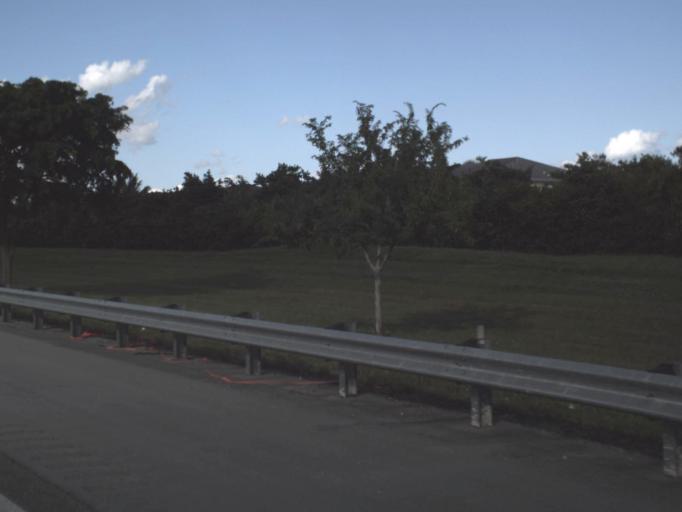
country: US
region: Florida
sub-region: Palm Beach County
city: Boca Pointe
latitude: 26.2953
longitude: -80.1691
